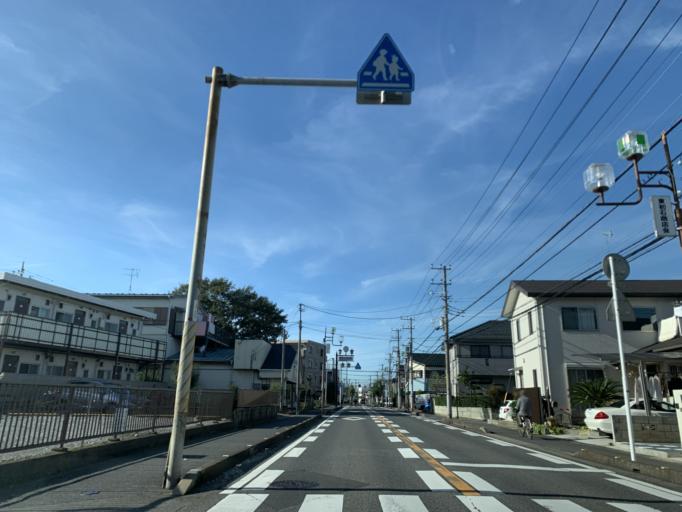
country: JP
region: Chiba
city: Nagareyama
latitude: 35.8840
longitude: 139.9226
